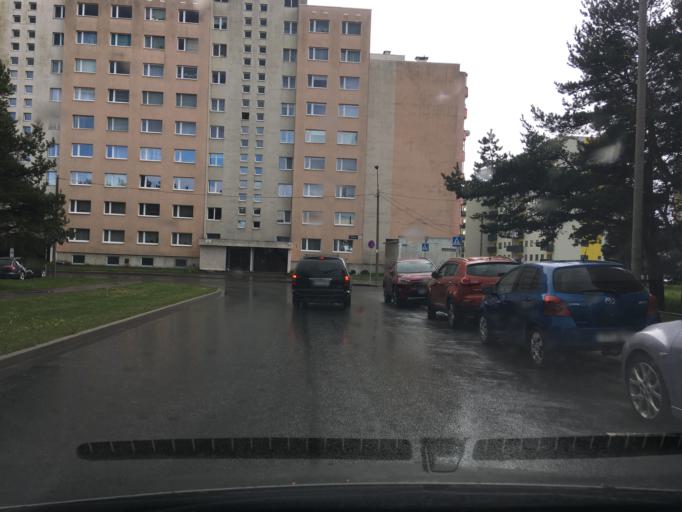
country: EE
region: Harju
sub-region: Tallinna linn
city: Kose
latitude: 59.4434
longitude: 24.8934
